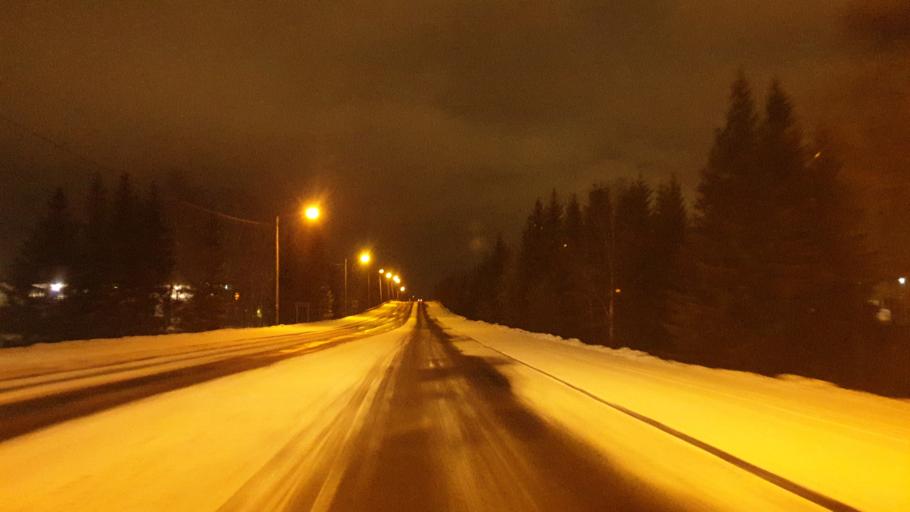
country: FI
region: Northern Ostrobothnia
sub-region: Oulu
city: Oulu
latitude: 64.9864
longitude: 25.4740
